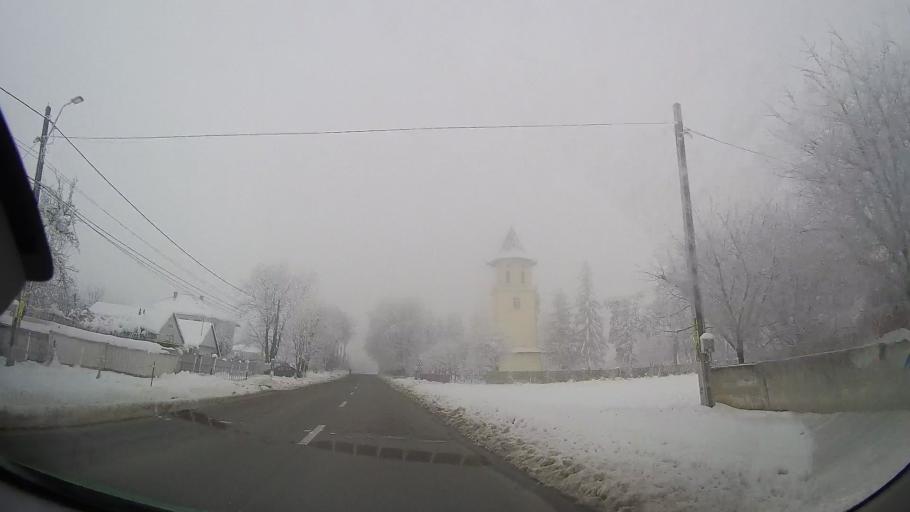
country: RO
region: Iasi
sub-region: Comuna Mogosesti-Siret
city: Mogosesti-Siret
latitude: 47.1649
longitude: 26.7700
